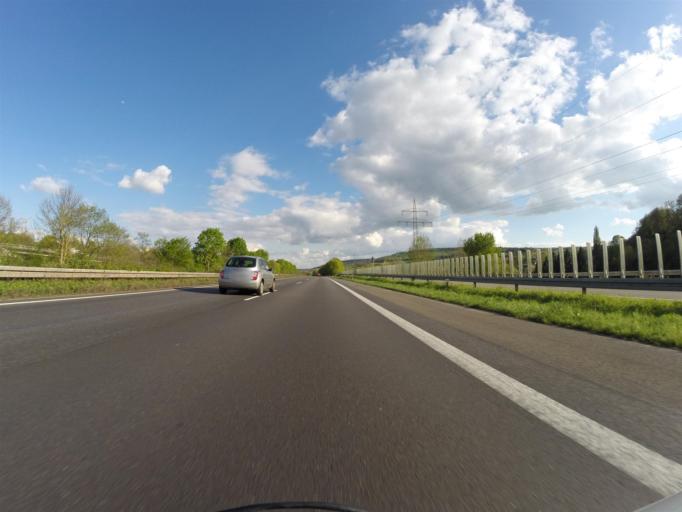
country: DE
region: Saarland
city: Merzig
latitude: 49.4236
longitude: 6.6323
